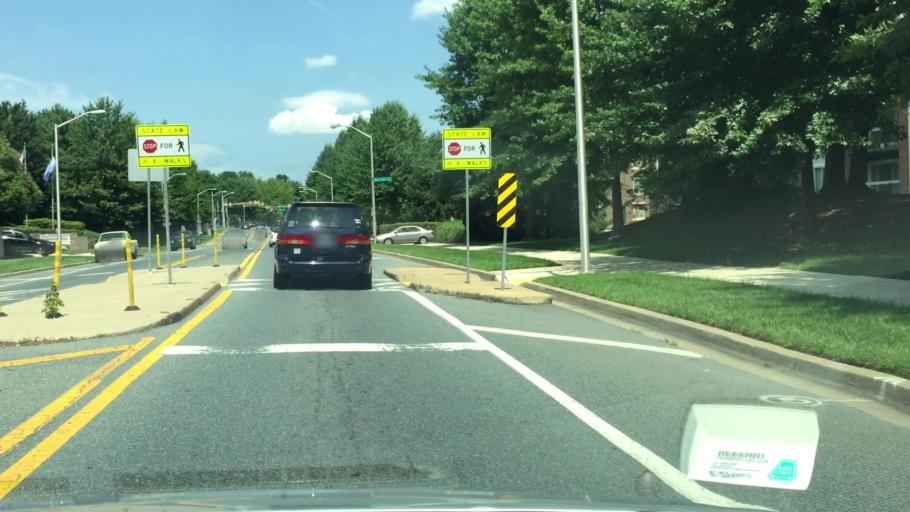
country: US
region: Maryland
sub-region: Montgomery County
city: Aspen Hill
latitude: 39.0896
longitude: -77.0715
